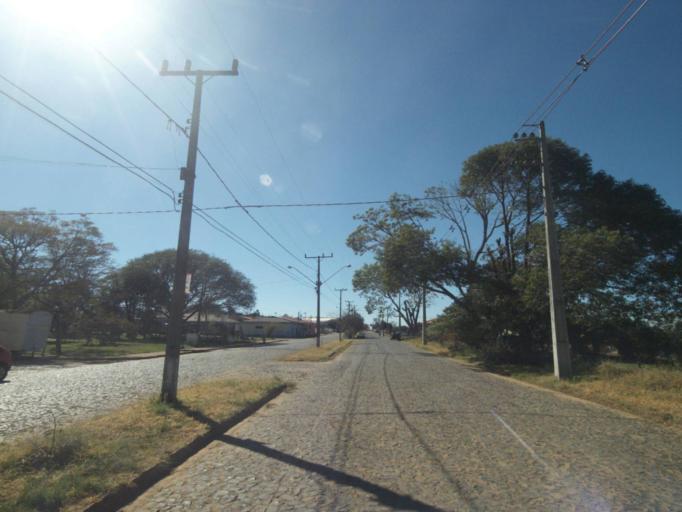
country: BR
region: Parana
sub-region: Reserva
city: Reserva
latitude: -24.6249
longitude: -50.6419
